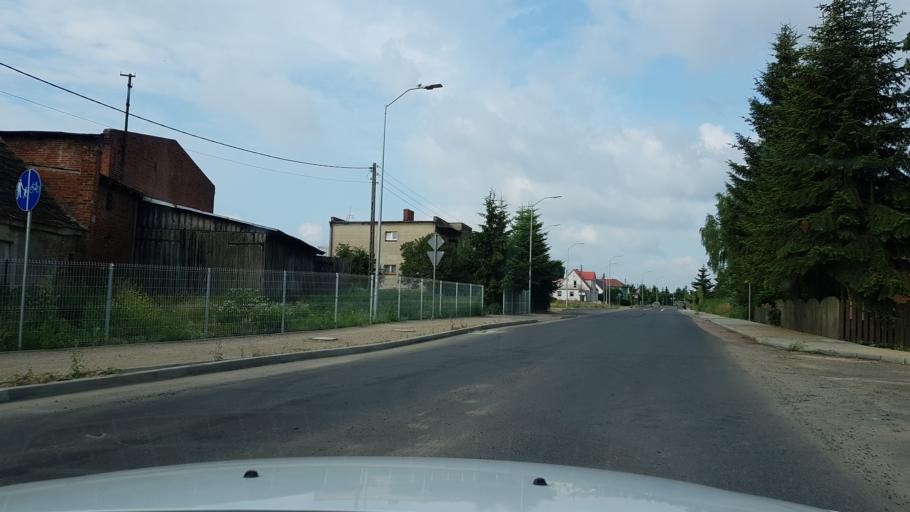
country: PL
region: West Pomeranian Voivodeship
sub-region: Powiat gryfinski
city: Gryfino
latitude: 53.2588
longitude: 14.5721
